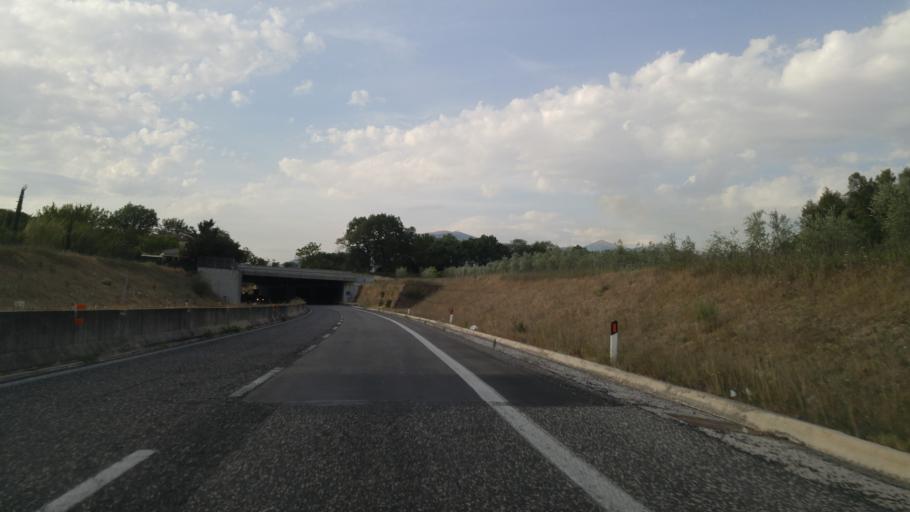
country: IT
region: Umbria
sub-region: Provincia di Perugia
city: San Giacomo
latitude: 42.7734
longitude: 12.7710
